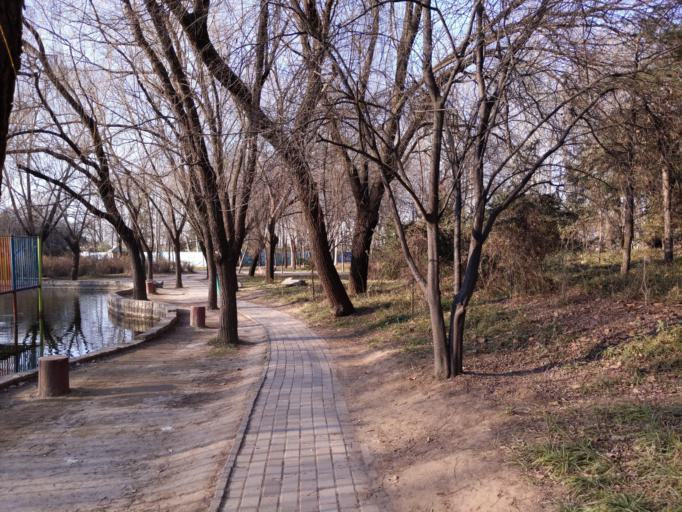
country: CN
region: Henan Sheng
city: Puyang
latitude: 35.7788
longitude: 114.9613
